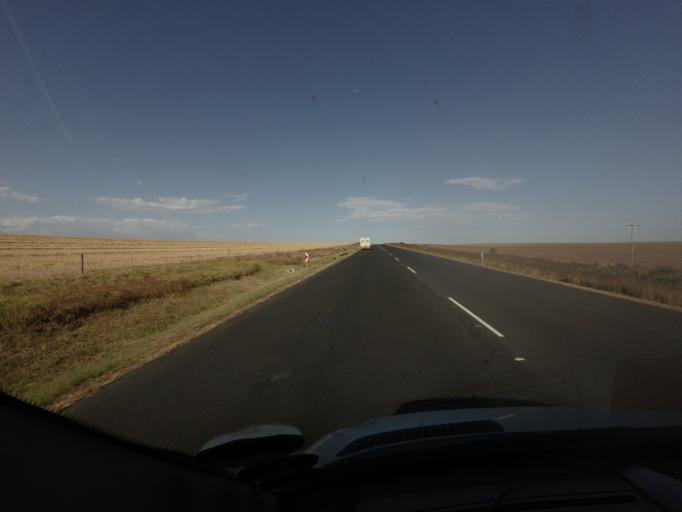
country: ZA
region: Western Cape
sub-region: Cape Winelands District Municipality
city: Ashton
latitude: -34.1409
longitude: 20.0139
